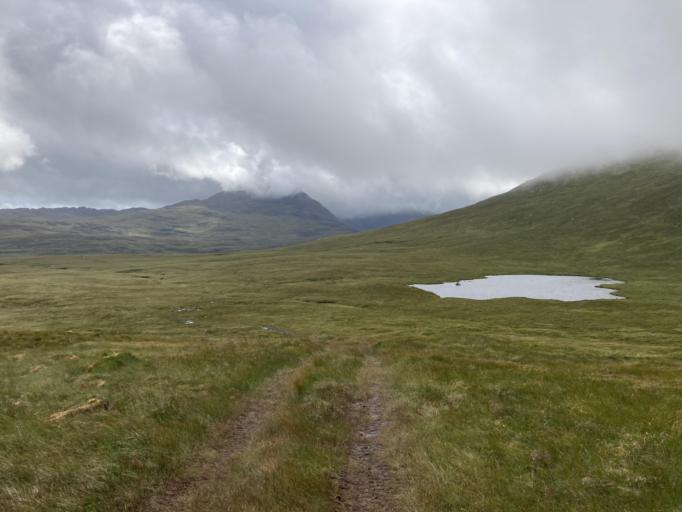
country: GB
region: Scotland
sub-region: Highland
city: Isle of Skye
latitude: 57.0135
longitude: -6.3772
